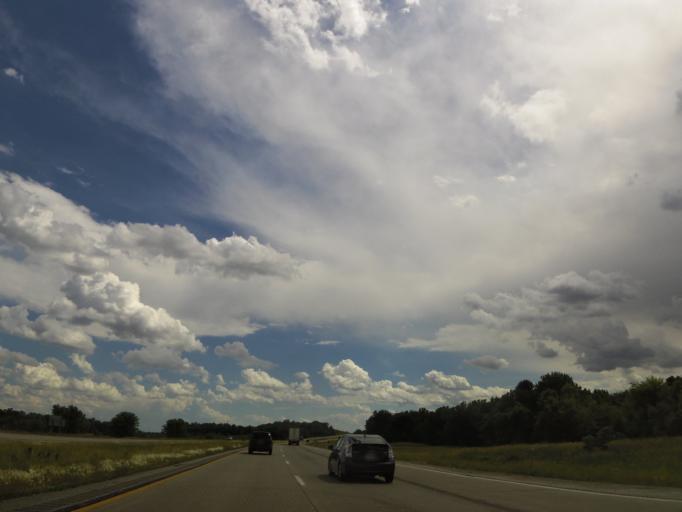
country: US
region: Iowa
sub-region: Johnson County
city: University Heights
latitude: 41.5503
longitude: -91.5447
